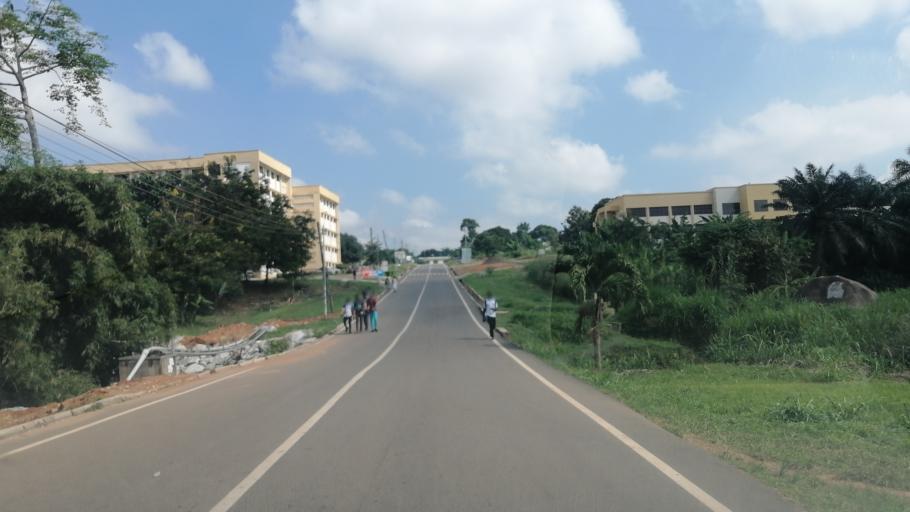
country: GH
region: Ashanti
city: Kumasi
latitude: 6.6992
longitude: -1.6820
